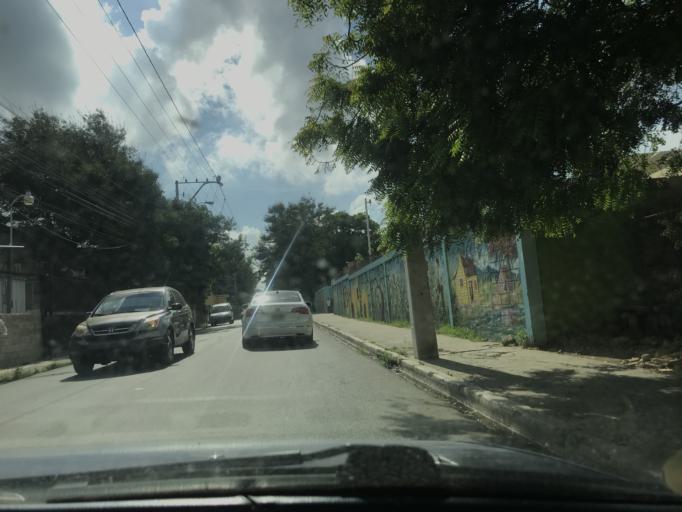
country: DO
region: Santiago
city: Santiago de los Caballeros
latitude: 19.4550
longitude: -70.7234
